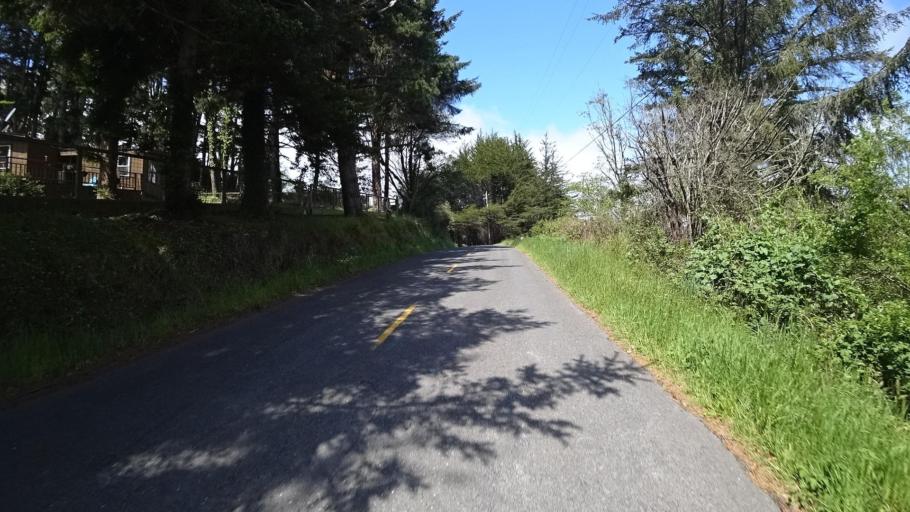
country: US
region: California
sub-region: Humboldt County
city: Humboldt Hill
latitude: 40.6728
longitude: -124.2170
